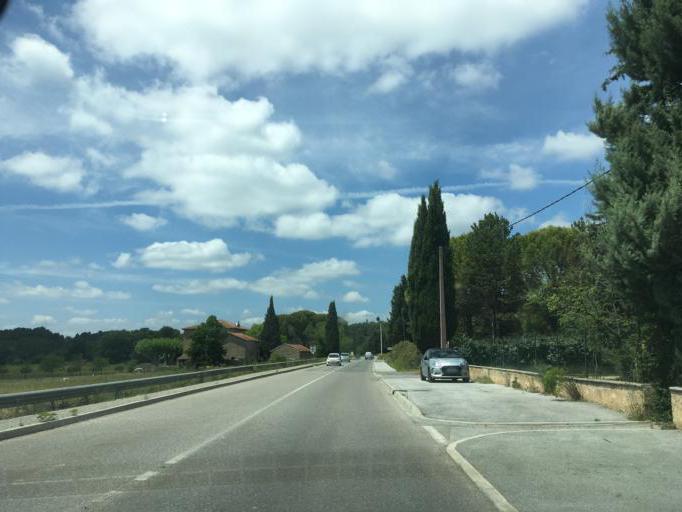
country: FR
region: Provence-Alpes-Cote d'Azur
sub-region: Departement du Var
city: Flayosc
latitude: 43.5394
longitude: 6.3802
